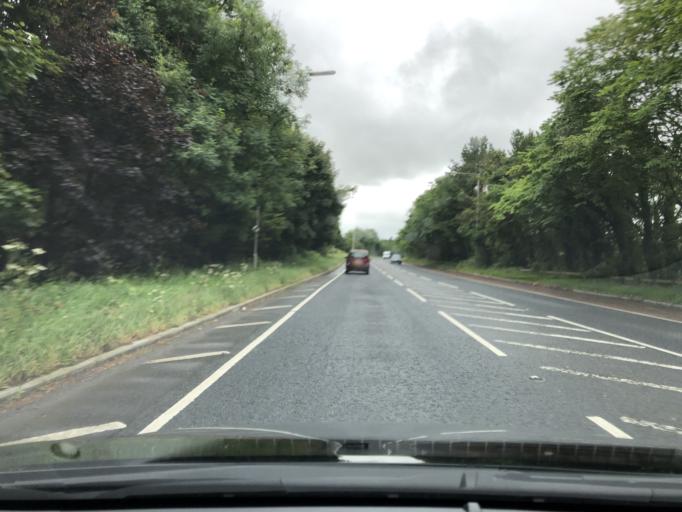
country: GB
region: Northern Ireland
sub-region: Down District
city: Dundrum
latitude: 54.3325
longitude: -5.8354
